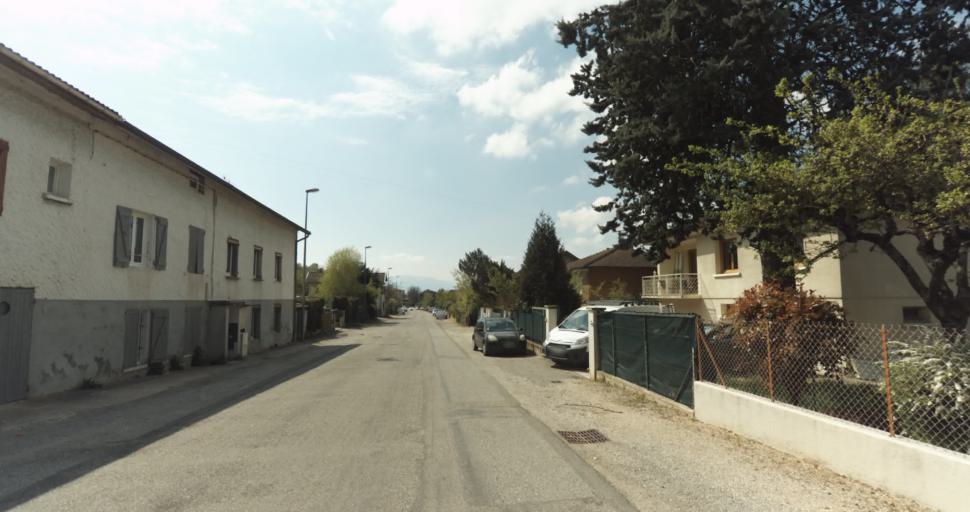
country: FR
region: Rhone-Alpes
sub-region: Departement de l'Isere
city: Saint-Marcellin
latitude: 45.1620
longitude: 5.3217
